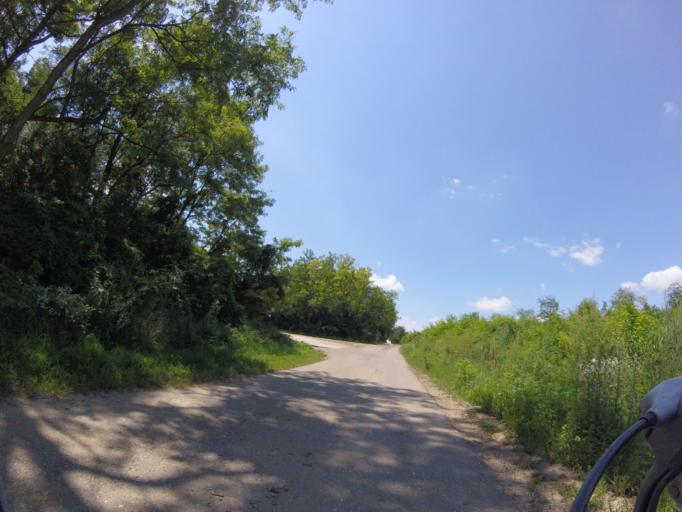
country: HU
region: Tolna
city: Iregszemcse
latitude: 46.6574
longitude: 18.1014
